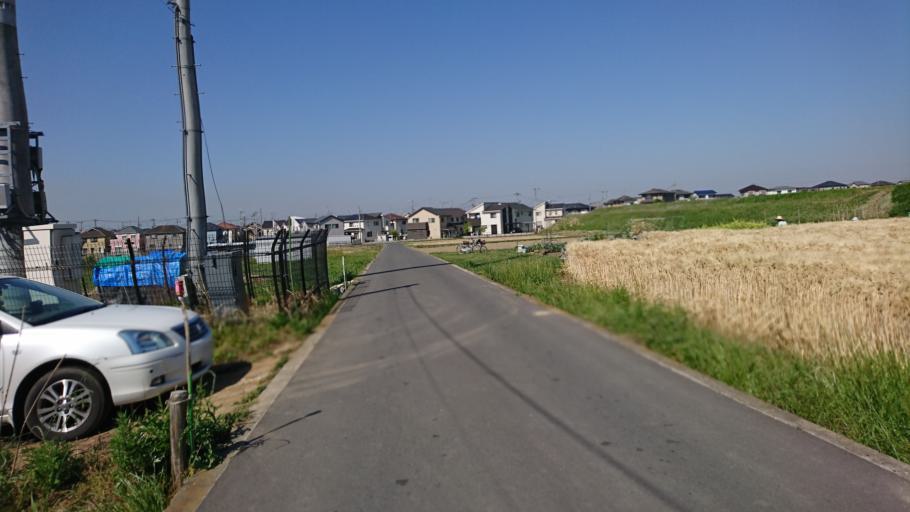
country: JP
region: Hyogo
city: Kakogawacho-honmachi
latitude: 34.7597
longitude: 134.8817
